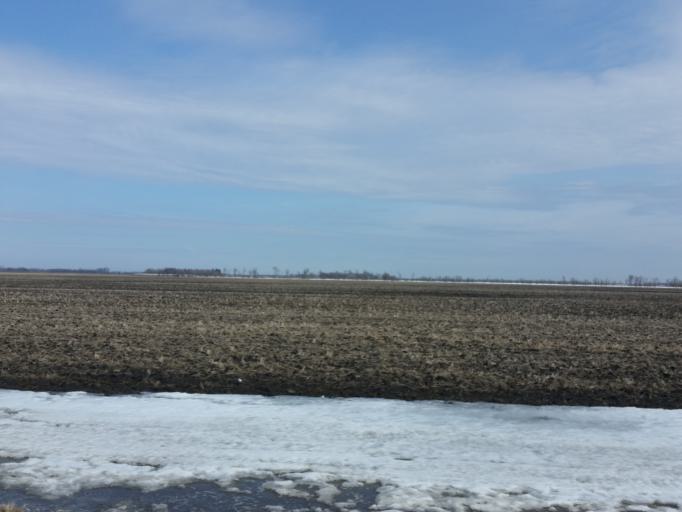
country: US
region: North Dakota
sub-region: Walsh County
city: Grafton
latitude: 48.4233
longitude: -97.2558
